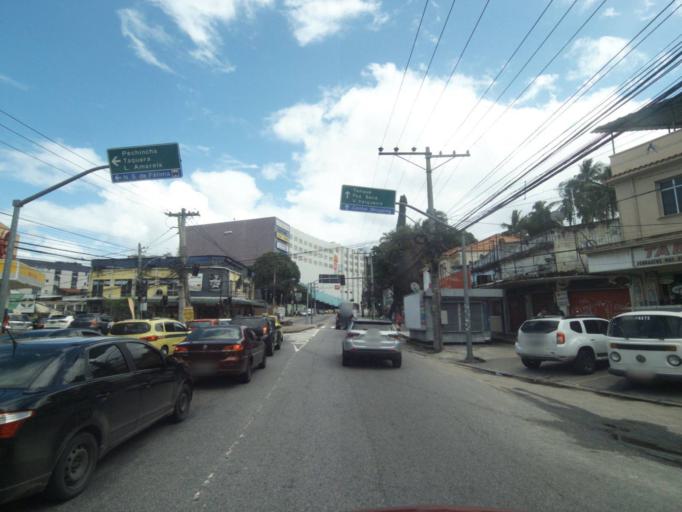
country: BR
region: Rio de Janeiro
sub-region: Sao Joao De Meriti
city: Sao Joao de Meriti
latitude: -22.9248
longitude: -43.3592
